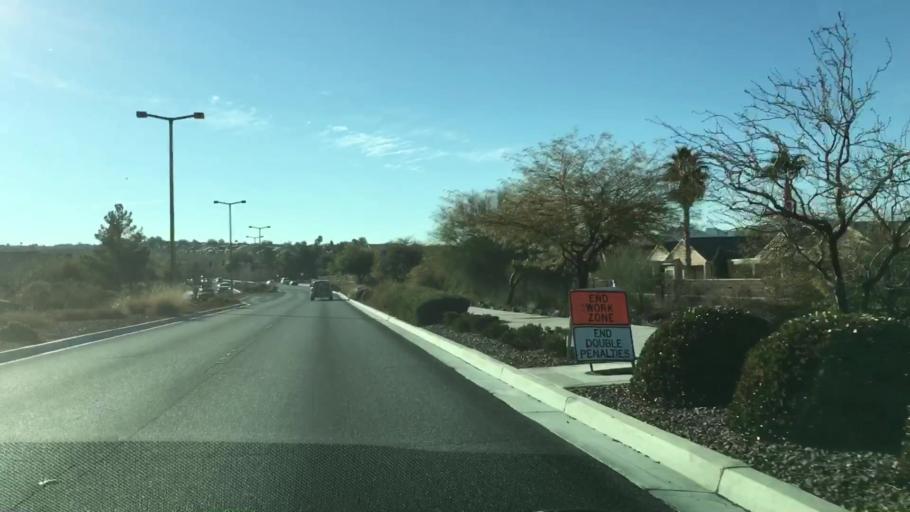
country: US
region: Nevada
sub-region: Clark County
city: Whitney
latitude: 35.9634
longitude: -115.1209
